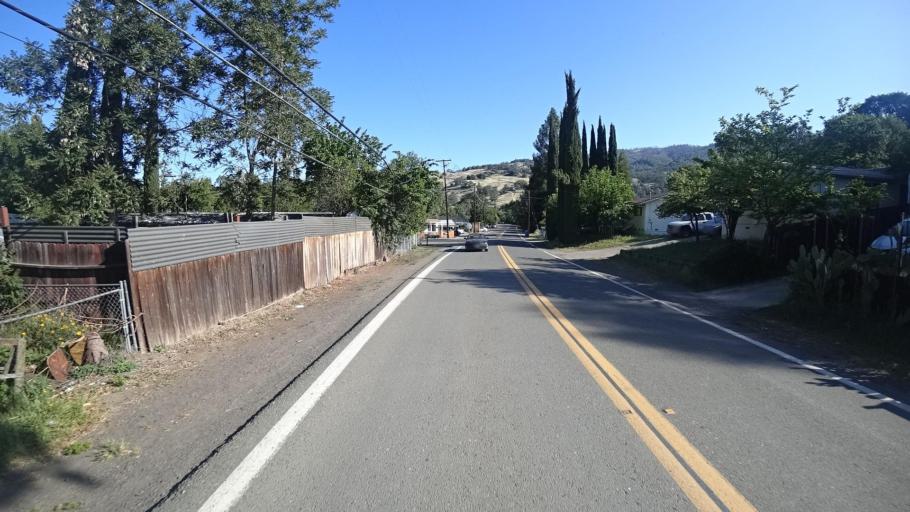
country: US
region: California
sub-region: Lake County
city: Lucerne
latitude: 39.0942
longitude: -122.7952
